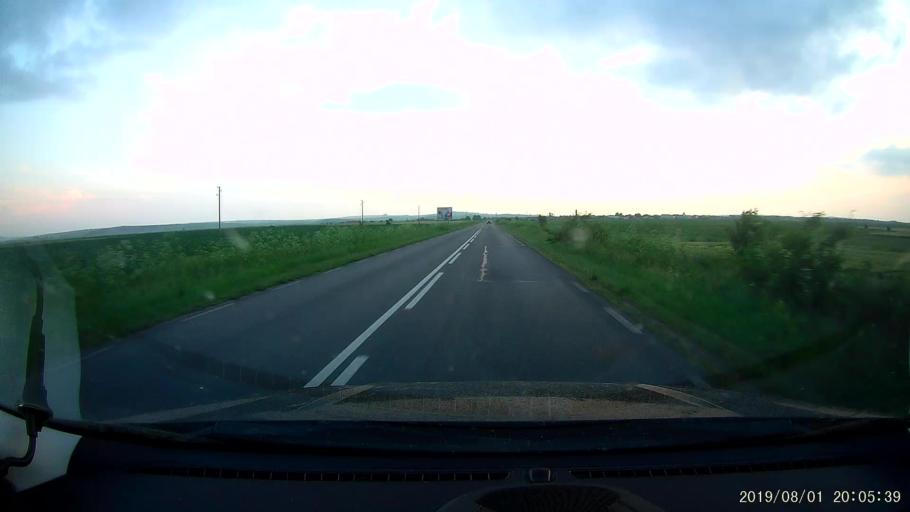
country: BG
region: Yambol
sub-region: Obshtina Yambol
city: Yambol
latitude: 42.5431
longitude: 26.5634
